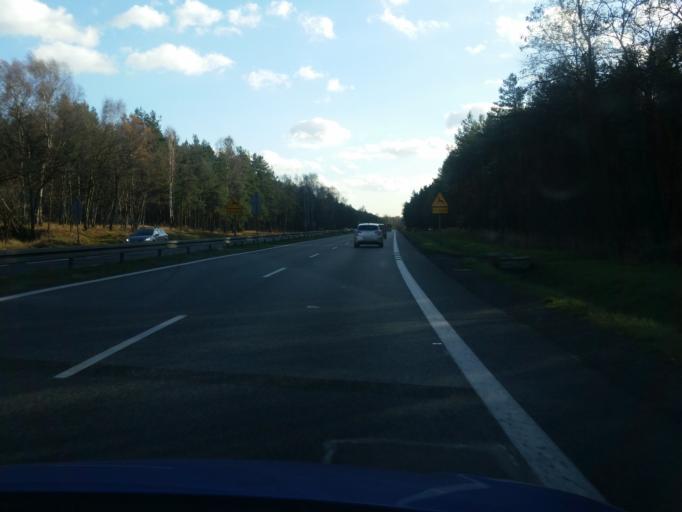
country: PL
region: Silesian Voivodeship
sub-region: Powiat myszkowski
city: Kozieglowy
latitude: 50.5325
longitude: 19.1902
